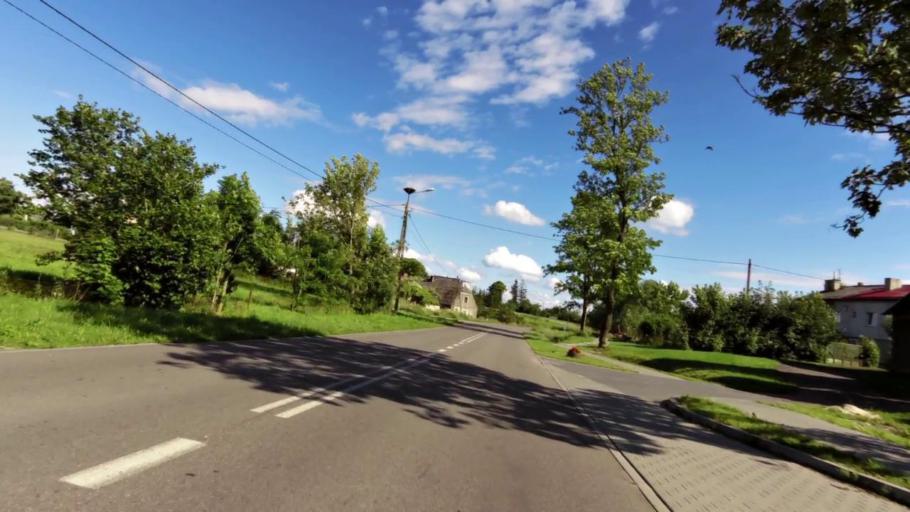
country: PL
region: West Pomeranian Voivodeship
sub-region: Powiat slawienski
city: Slawno
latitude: 54.4587
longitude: 16.7369
